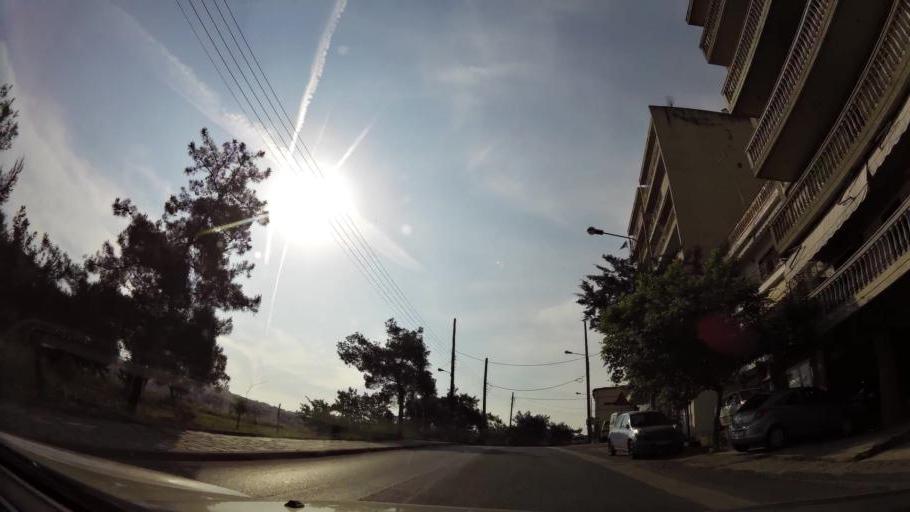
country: GR
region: Central Macedonia
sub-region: Nomos Thessalonikis
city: Polichni
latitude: 40.6581
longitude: 22.9493
